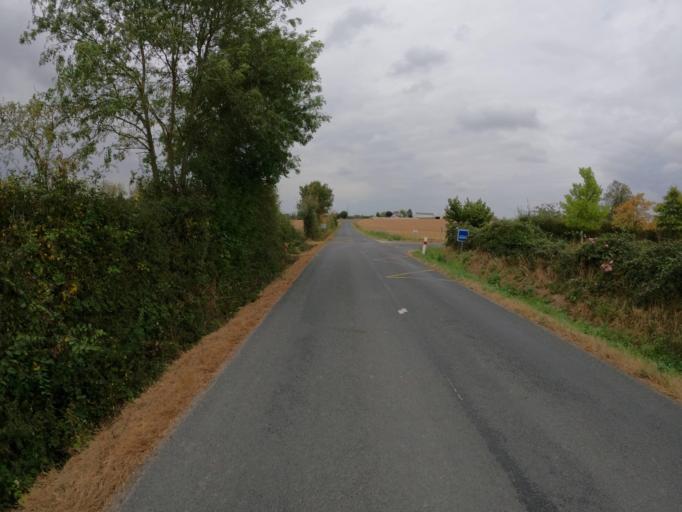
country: FR
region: Pays de la Loire
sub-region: Departement de la Vendee
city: Les Landes-Genusson
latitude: 46.9774
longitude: -1.1123
